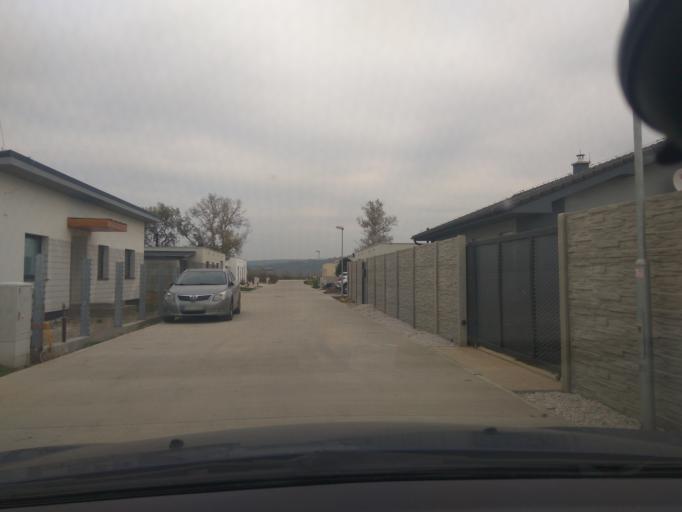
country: SK
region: Trnavsky
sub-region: Okres Trnava
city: Piestany
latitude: 48.6090
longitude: 17.8616
